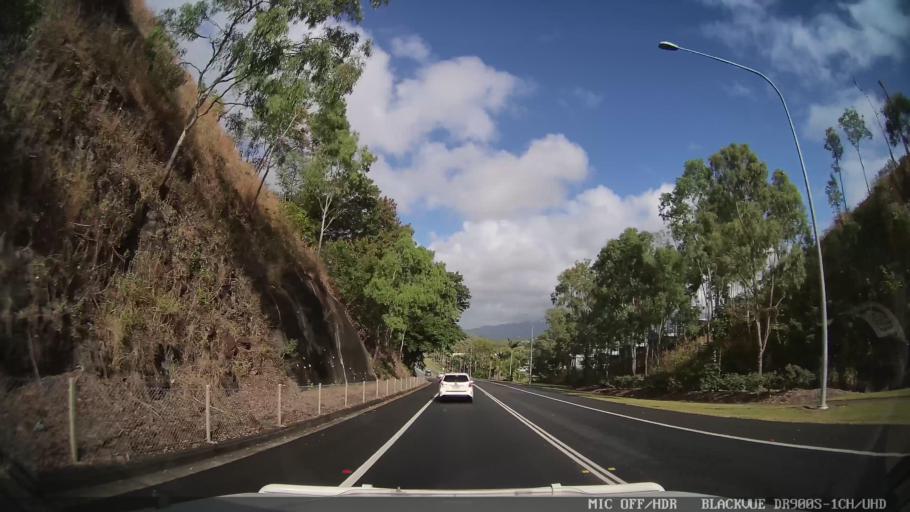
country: AU
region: Queensland
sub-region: Whitsunday
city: Proserpine
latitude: -20.2717
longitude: 148.7075
